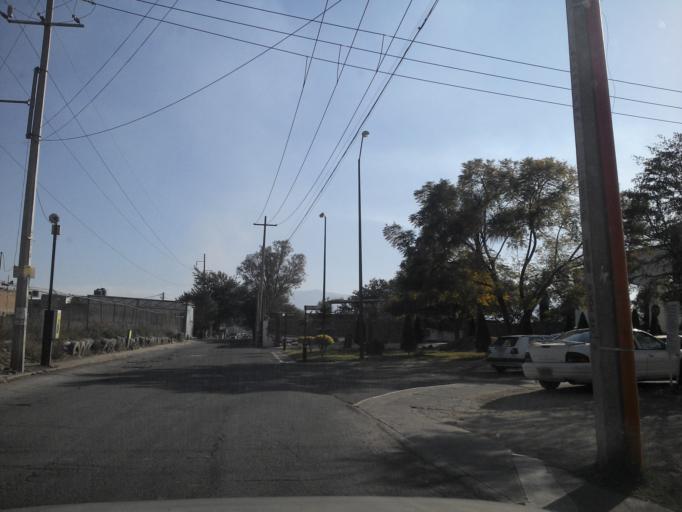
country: MX
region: Jalisco
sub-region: San Pedro Tlaquepaque
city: Paseo del Prado
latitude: 20.5909
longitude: -103.3898
